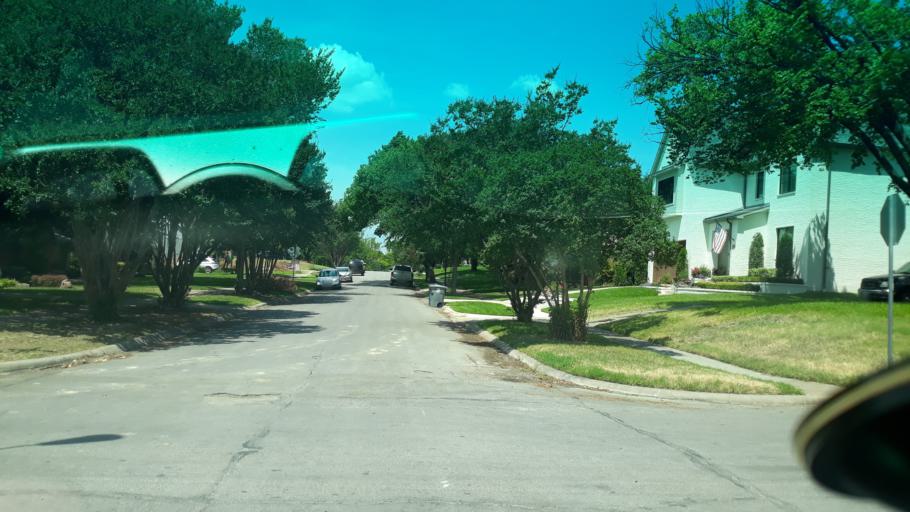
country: US
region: Texas
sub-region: Dallas County
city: Highland Park
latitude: 32.8123
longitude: -96.7411
